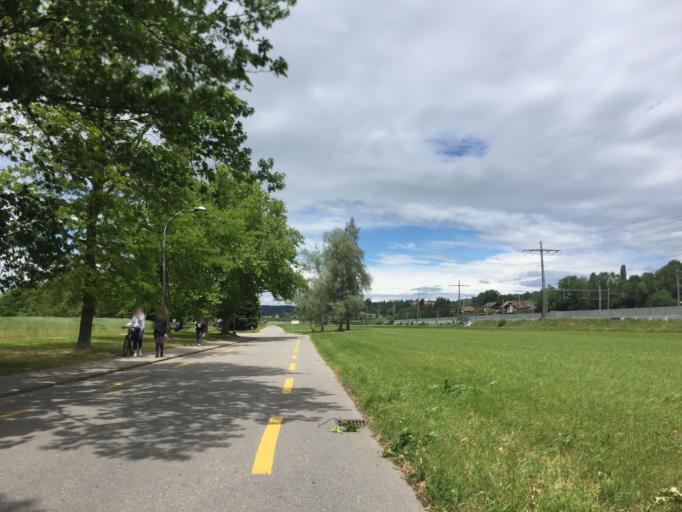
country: CH
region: Bern
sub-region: Bern-Mittelland District
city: Munsingen
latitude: 46.8772
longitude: 7.5569
